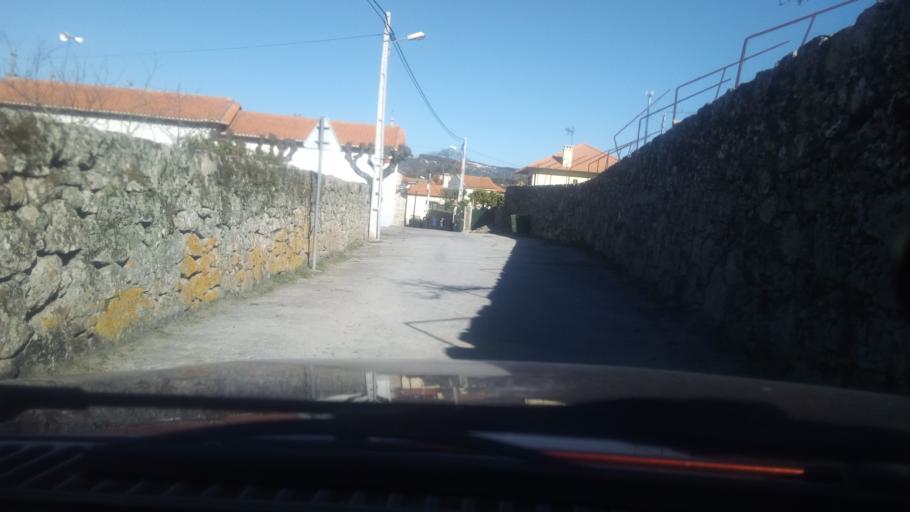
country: PT
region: Guarda
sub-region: Fornos de Algodres
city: Fornos de Algodres
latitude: 40.6079
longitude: -7.5069
